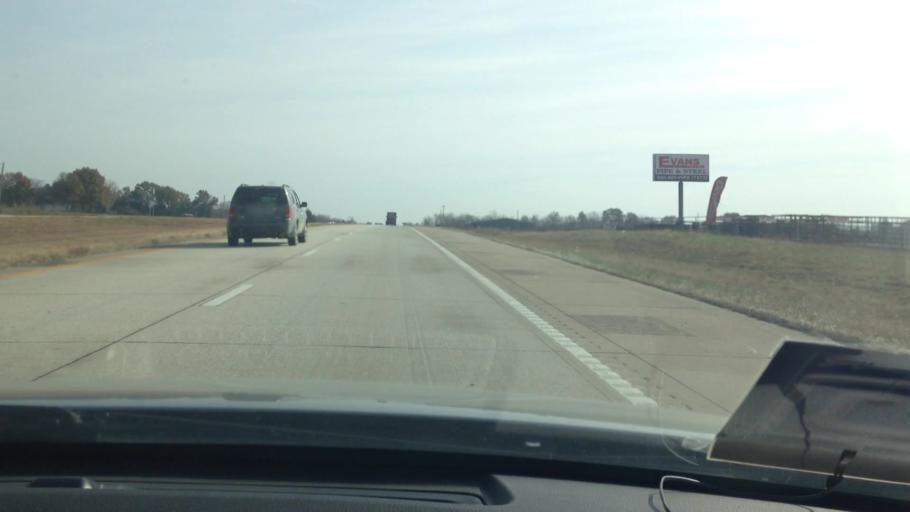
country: US
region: Missouri
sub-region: Henry County
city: Clinton
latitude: 38.4157
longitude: -93.8613
